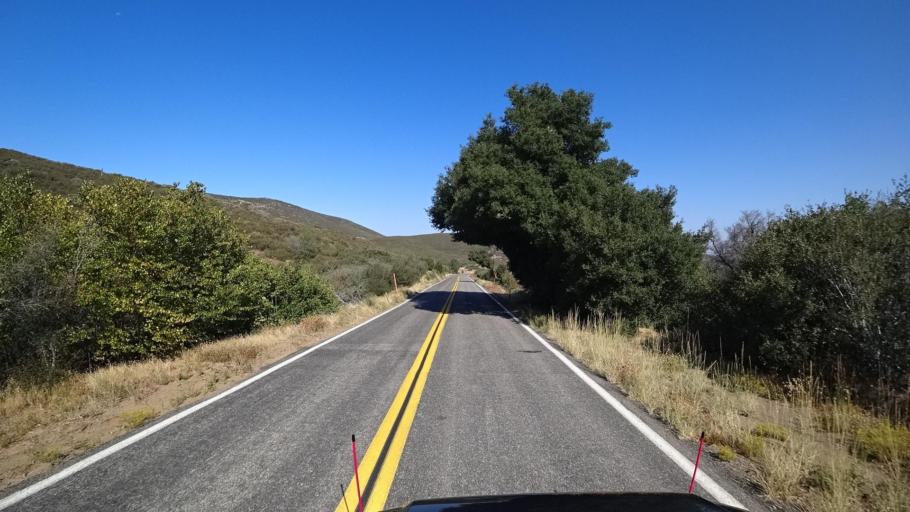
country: US
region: California
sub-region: San Diego County
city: Julian
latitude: 32.9827
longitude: -116.5319
